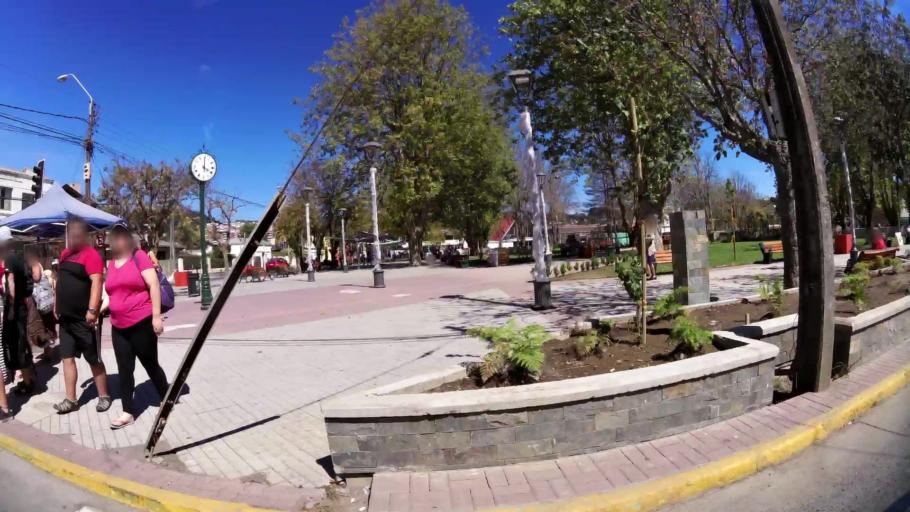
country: CL
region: Biobio
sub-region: Provincia de Concepcion
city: Penco
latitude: -36.7381
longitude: -72.9934
